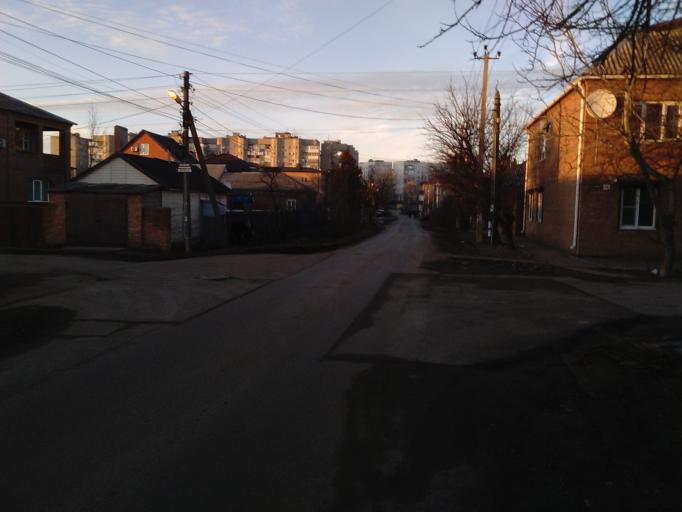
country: RU
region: Rostov
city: Bataysk
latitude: 47.1522
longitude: 39.7407
